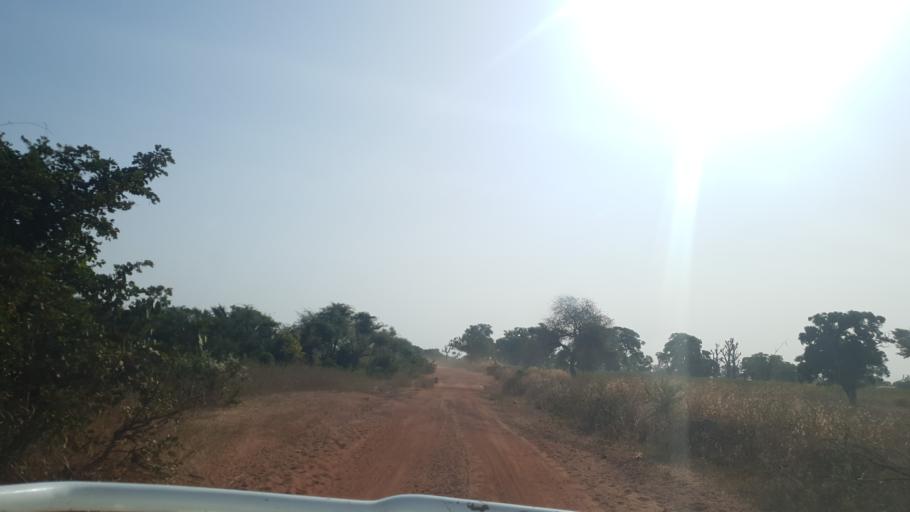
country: ML
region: Koulikoro
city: Dioila
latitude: 12.7077
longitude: -6.7767
